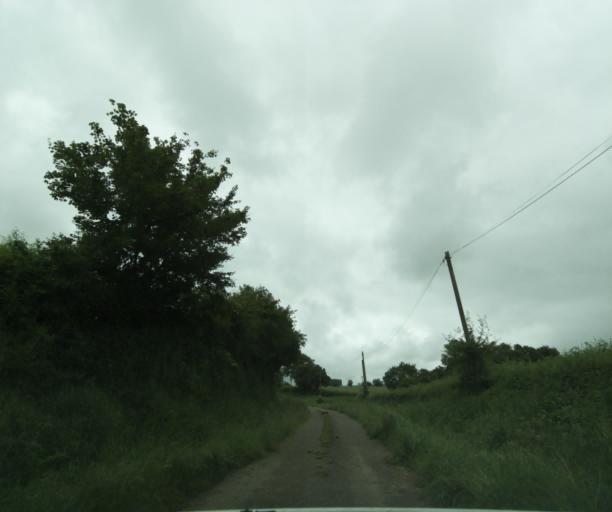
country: FR
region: Bourgogne
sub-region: Departement de Saone-et-Loire
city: Charolles
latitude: 46.4859
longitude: 4.3221
